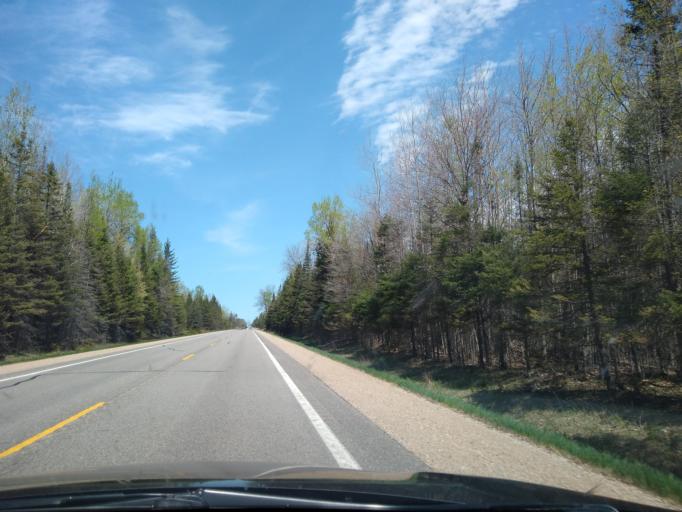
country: US
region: Michigan
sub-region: Delta County
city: Gladstone
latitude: 46.0517
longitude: -86.9813
